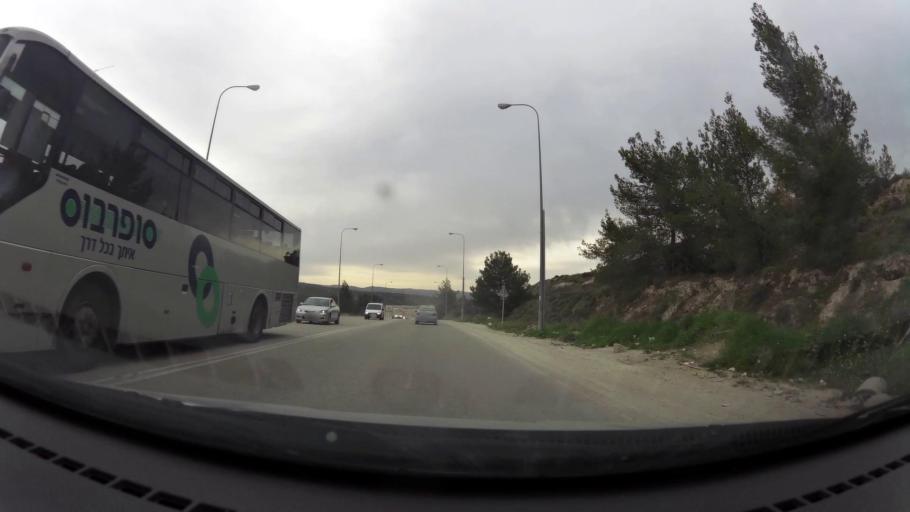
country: IL
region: Jerusalem
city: Bet Shemesh
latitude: 31.7053
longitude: 35.0035
